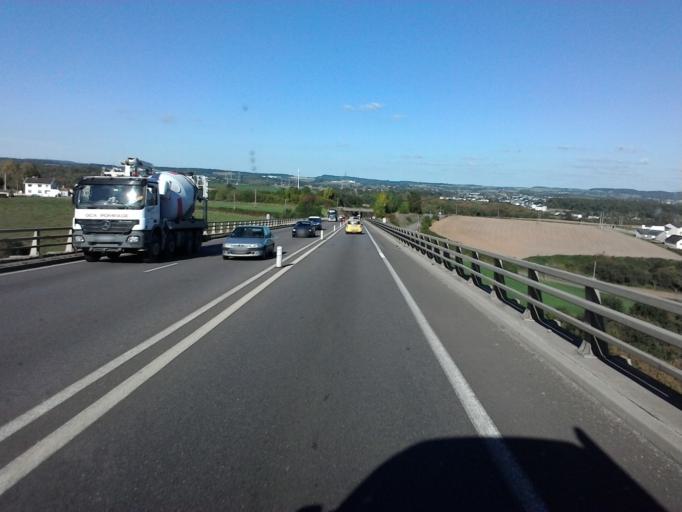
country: FR
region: Lorraine
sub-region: Departement de Meurthe-et-Moselle
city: Mont-Saint-Martin
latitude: 49.5455
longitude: 5.7687
